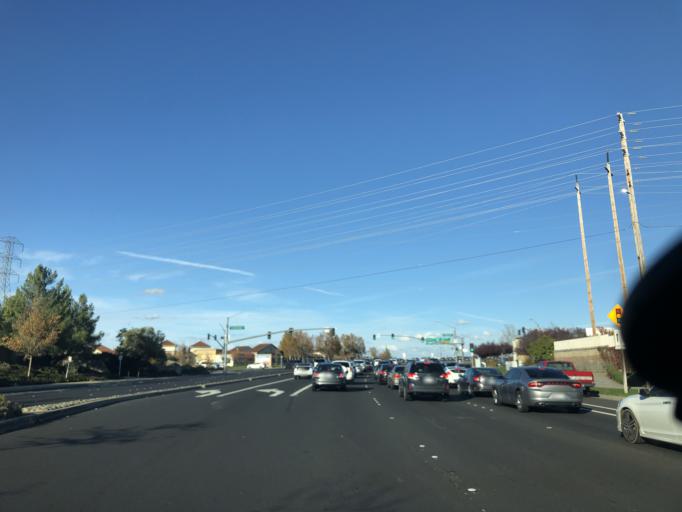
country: US
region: California
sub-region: Placer County
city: Roseville
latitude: 38.7822
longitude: -121.2871
